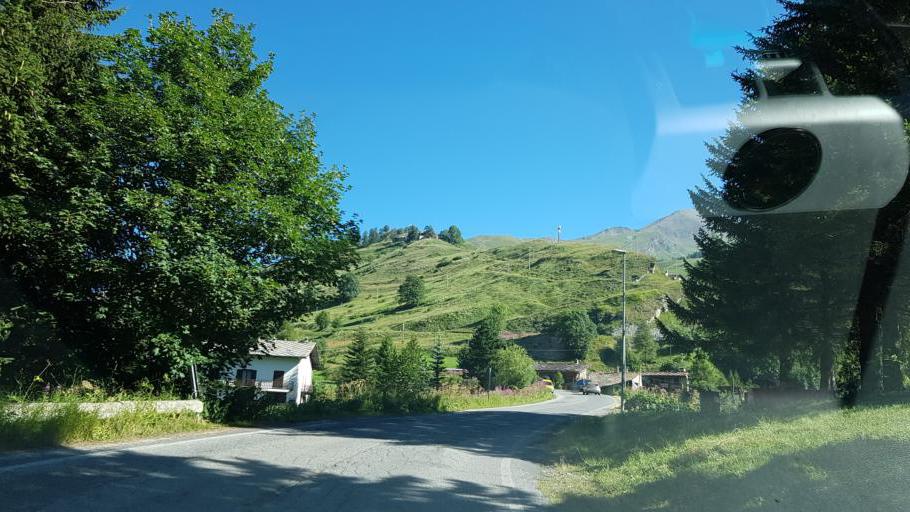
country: IT
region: Piedmont
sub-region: Provincia di Cuneo
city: Pontechianale
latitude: 44.6245
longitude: 7.0230
